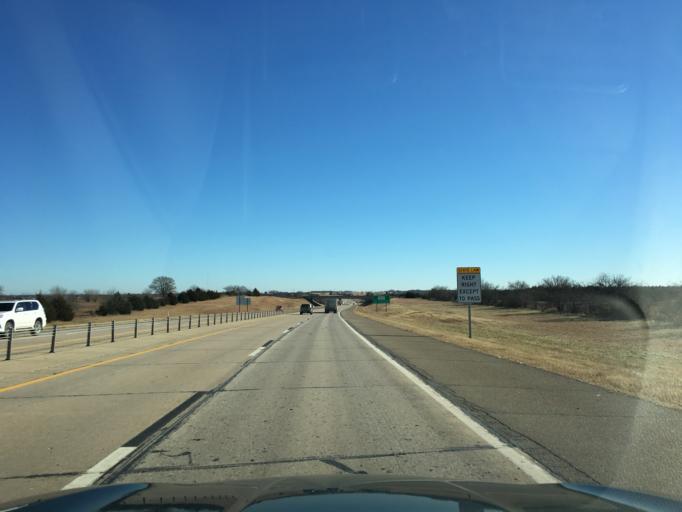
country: US
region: Oklahoma
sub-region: Pawnee County
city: Pawnee
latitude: 36.2355
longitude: -96.9207
